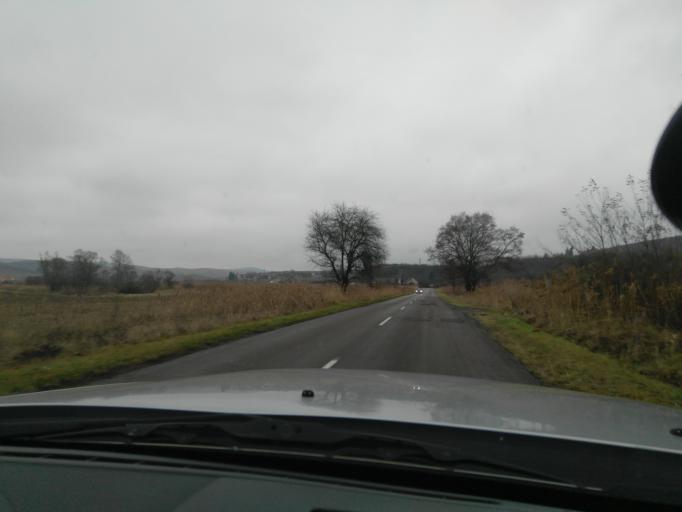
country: HU
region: Nograd
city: Matraterenye
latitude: 48.0427
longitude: 19.9206
